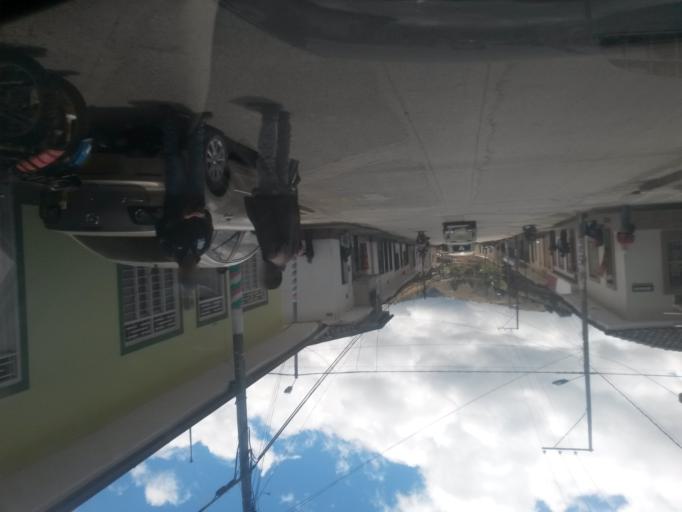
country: CO
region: Cauca
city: Silvia
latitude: 2.6136
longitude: -76.3760
